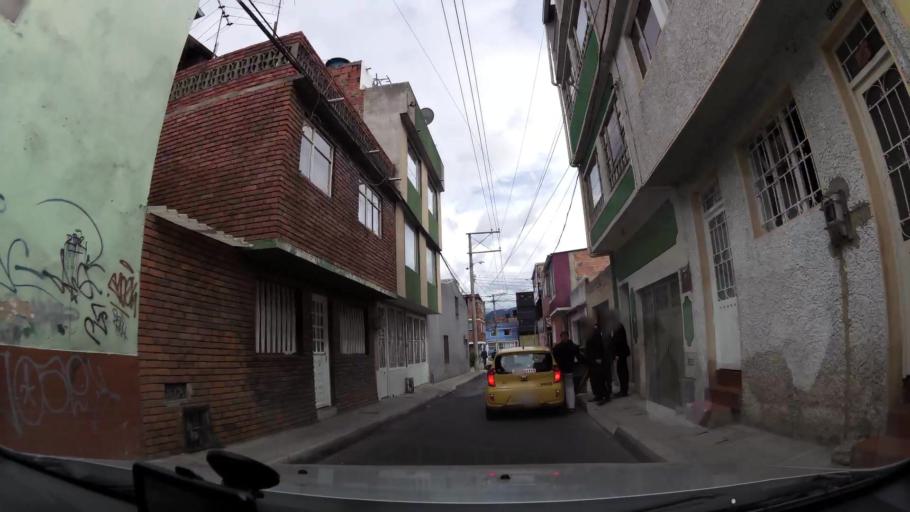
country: CO
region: Bogota D.C.
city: Bogota
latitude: 4.5992
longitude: -74.1281
